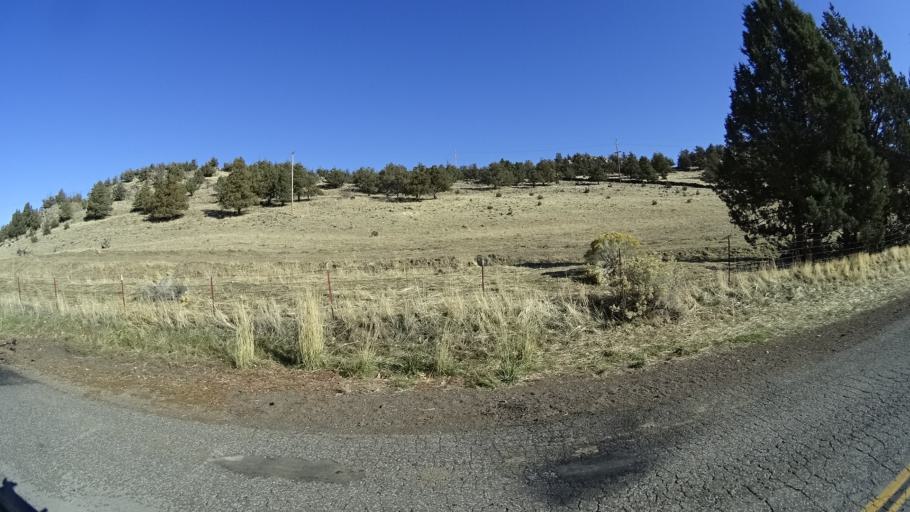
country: US
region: California
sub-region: Siskiyou County
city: Montague
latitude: 41.6900
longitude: -122.3713
